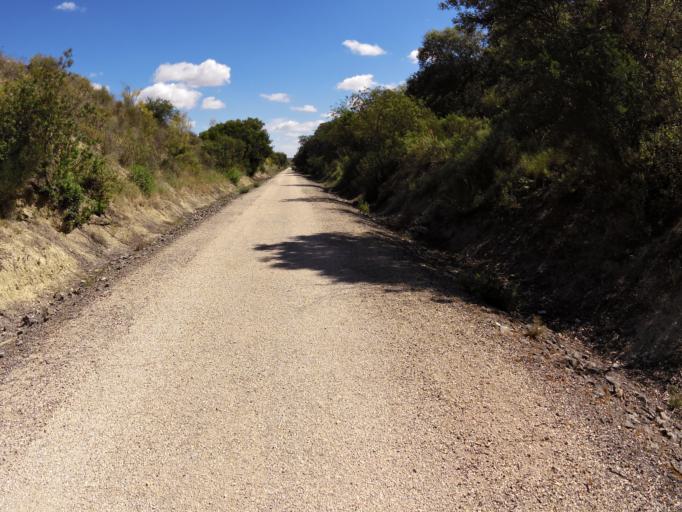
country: ES
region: Andalusia
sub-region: Provincia de Jaen
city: Alcaudete
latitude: 37.6248
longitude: -4.0923
